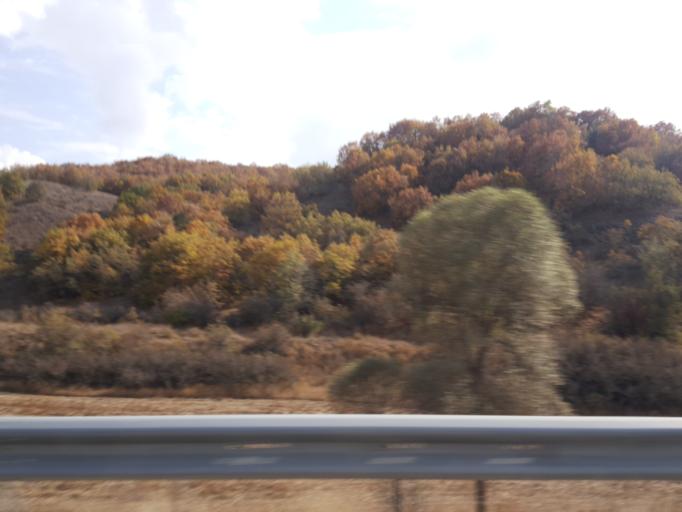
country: TR
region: Corum
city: Alaca
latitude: 40.3341
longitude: 34.7142
